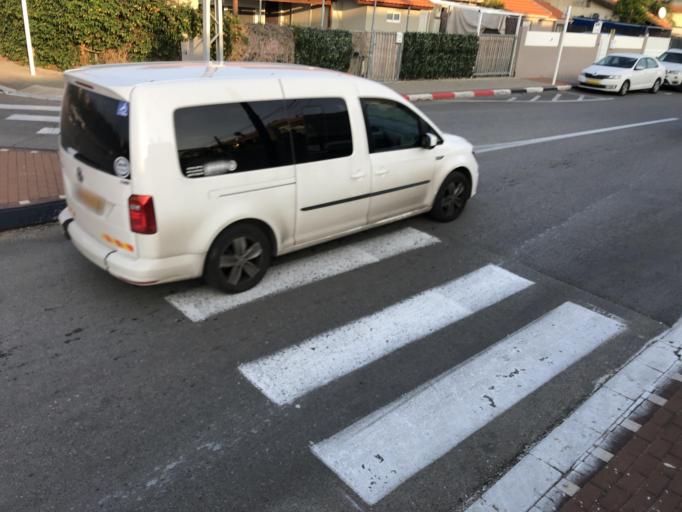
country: IL
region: Northern District
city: `Akko
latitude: 32.9282
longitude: 35.0888
